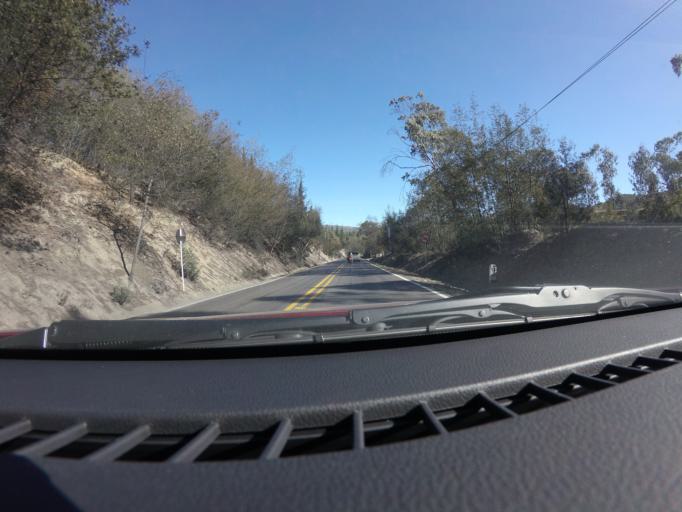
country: CO
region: Cundinamarca
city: Sutatausa
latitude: 5.2404
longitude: -73.8558
